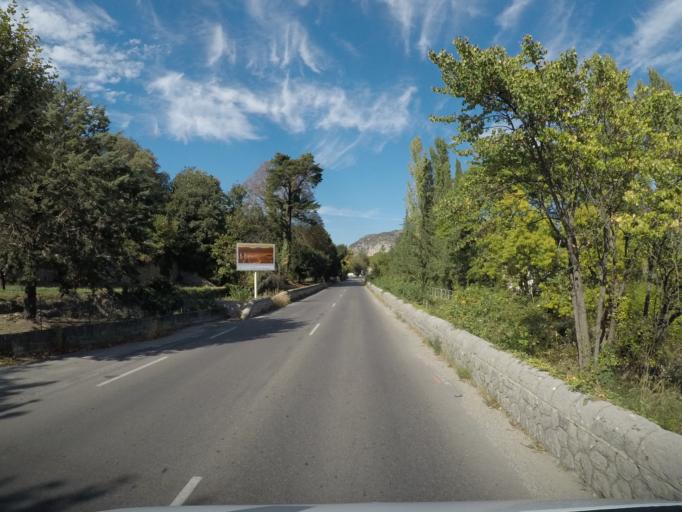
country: FR
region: Languedoc-Roussillon
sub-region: Departement du Gard
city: Anduze
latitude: 44.0448
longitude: 3.9848
